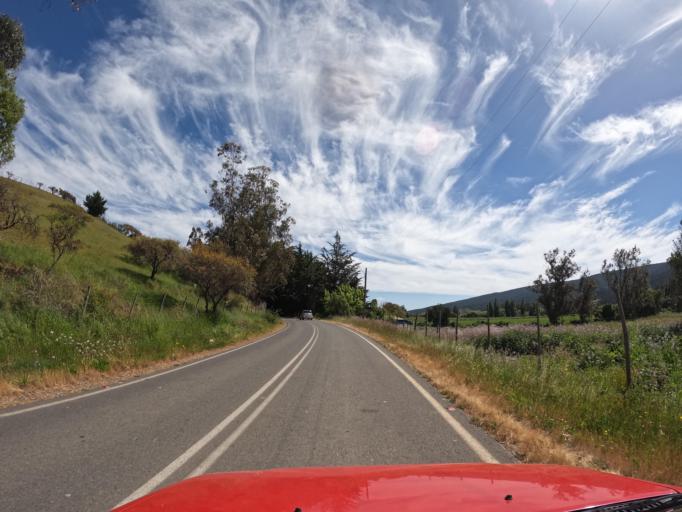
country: CL
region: Maule
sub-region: Provincia de Talca
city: Constitucion
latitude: -35.0104
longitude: -72.0357
